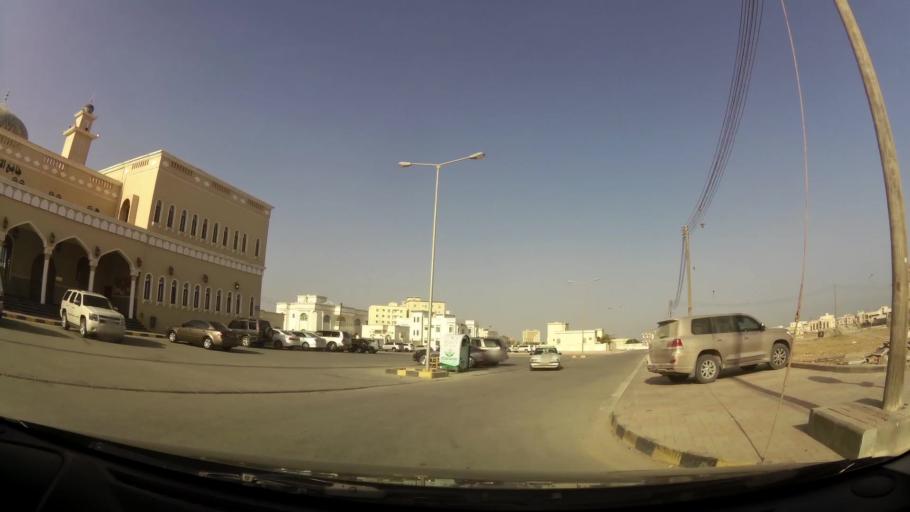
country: OM
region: Zufar
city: Salalah
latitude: 17.0216
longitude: 54.0292
